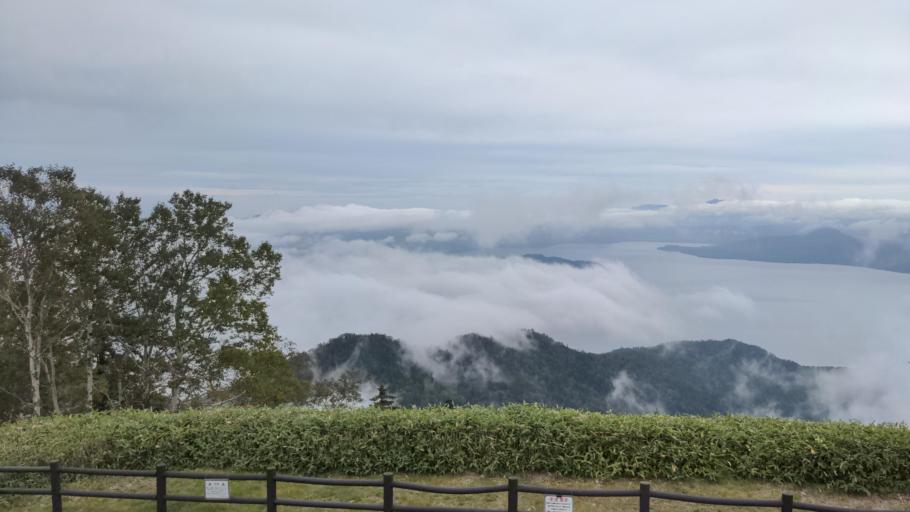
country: JP
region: Hokkaido
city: Bihoro
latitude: 43.5773
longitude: 144.2243
